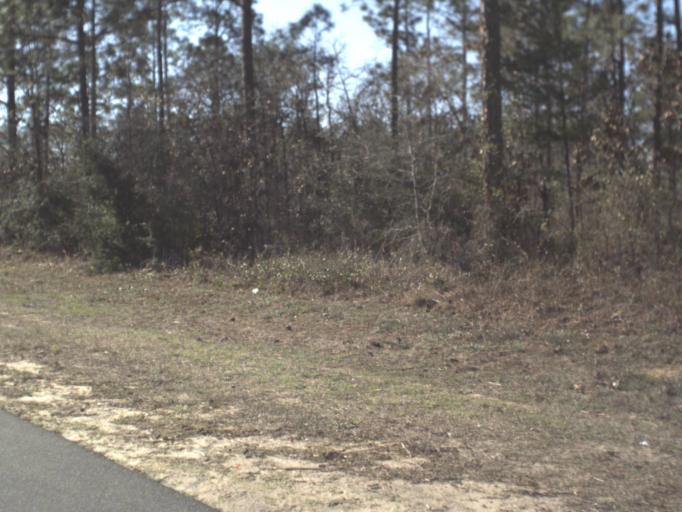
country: US
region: Florida
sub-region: Bay County
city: Youngstown
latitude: 30.4363
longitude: -85.3510
